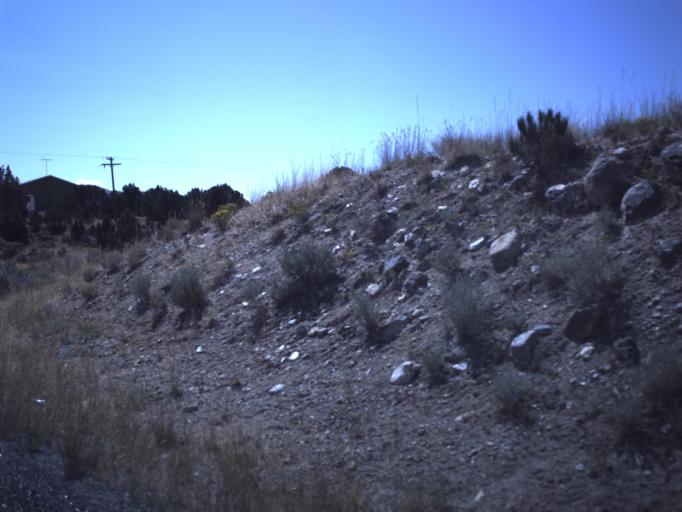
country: US
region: Utah
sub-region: Utah County
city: Genola
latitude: 39.9293
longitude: -112.1646
